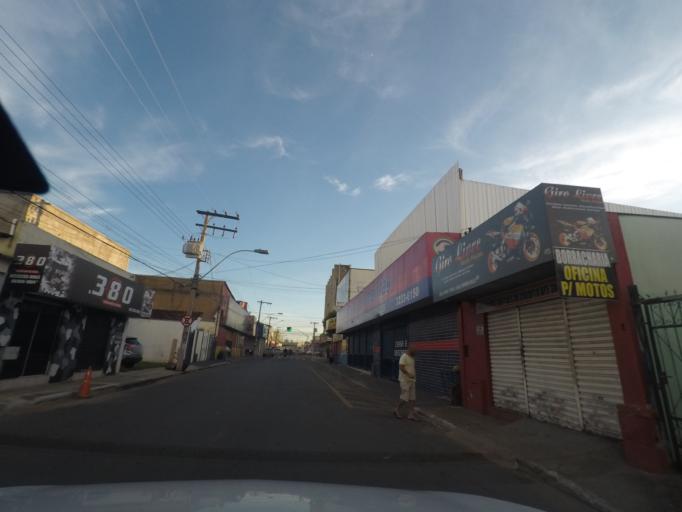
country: BR
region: Goias
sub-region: Goiania
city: Goiania
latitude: -16.6758
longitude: -49.2889
